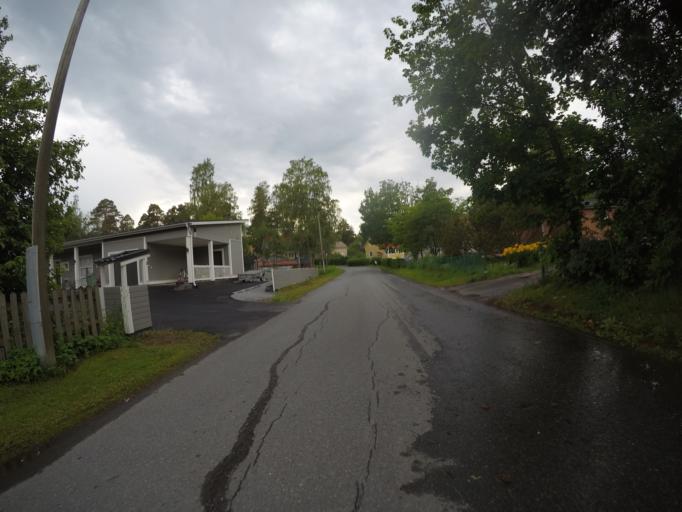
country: FI
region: Haeme
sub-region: Haemeenlinna
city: Haemeenlinna
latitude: 61.0079
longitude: 24.4922
